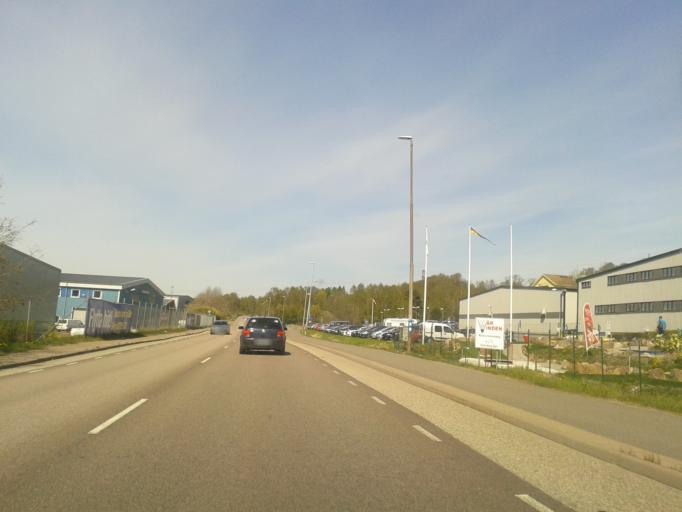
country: SE
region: Vaestra Goetaland
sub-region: Goteborg
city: Eriksbo
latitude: 57.7541
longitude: 12.0112
